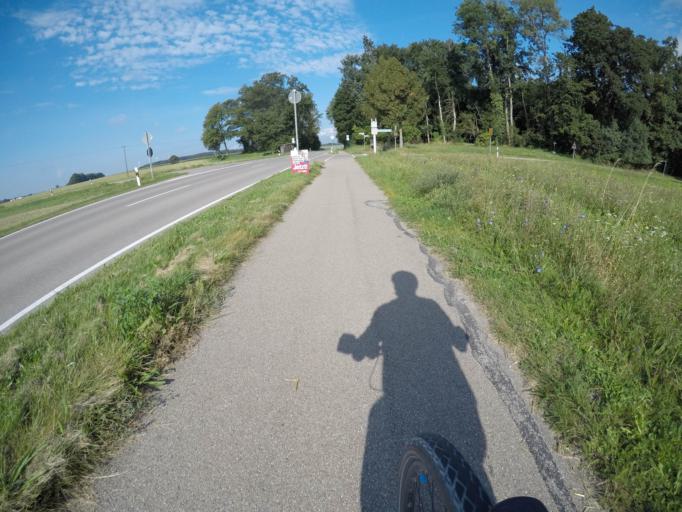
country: DE
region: Bavaria
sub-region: Swabia
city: Ehingen
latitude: 48.6040
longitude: 10.8103
